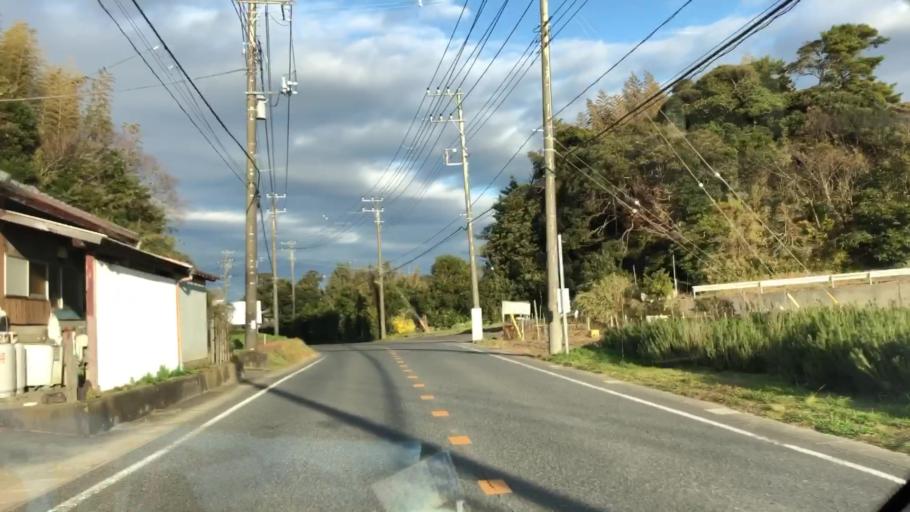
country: JP
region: Chiba
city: Tateyama
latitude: 34.9809
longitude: 139.9489
